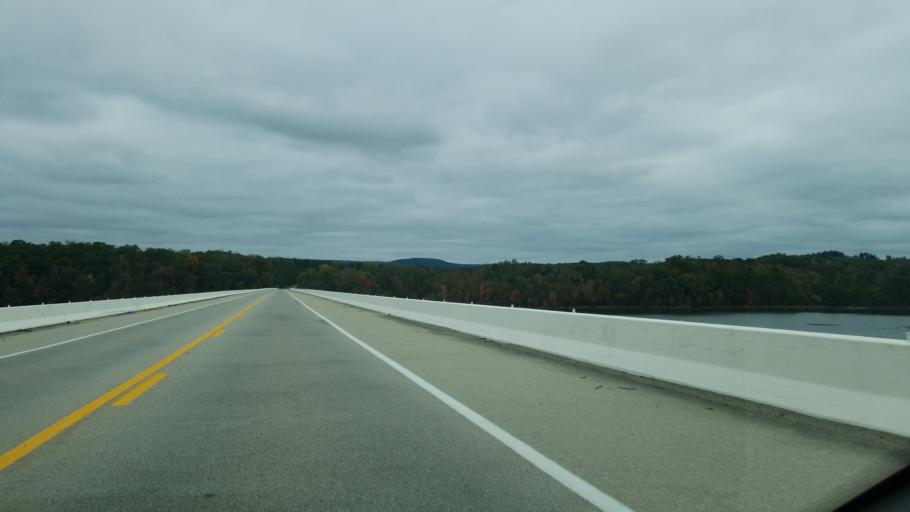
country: US
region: Tennessee
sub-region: Rhea County
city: Graysville
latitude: 35.4095
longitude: -85.0188
